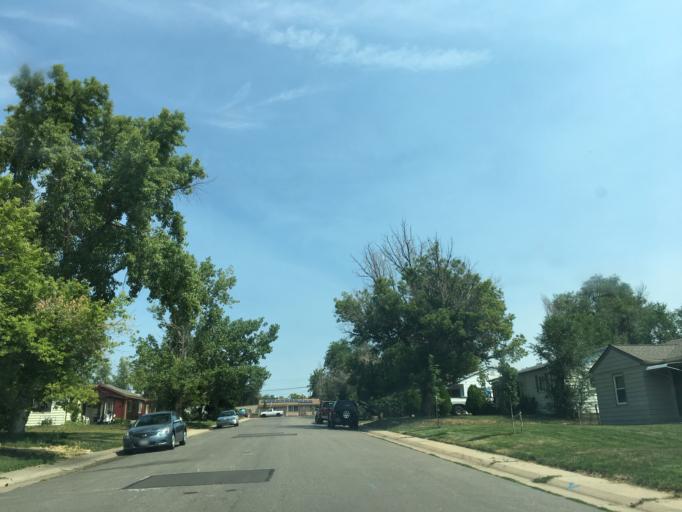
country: US
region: Colorado
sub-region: Jefferson County
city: Lakewood
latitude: 39.6957
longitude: -105.0496
